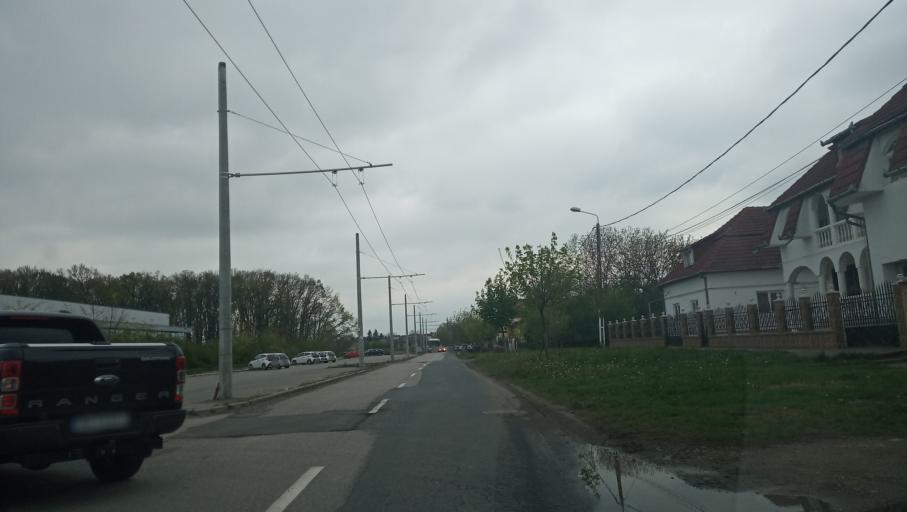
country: RO
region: Timis
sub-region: Comuna Ghiroda
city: Ghiroda
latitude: 45.7670
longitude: 21.2686
